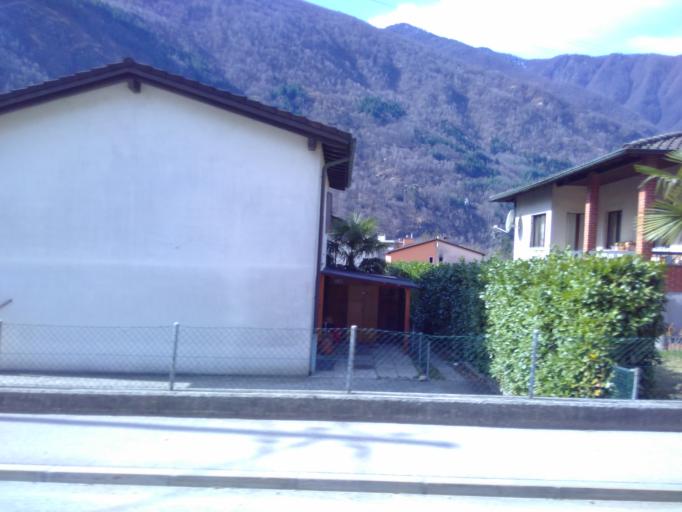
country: CH
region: Ticino
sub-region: Locarno District
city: Verscio
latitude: 46.2256
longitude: 8.7418
